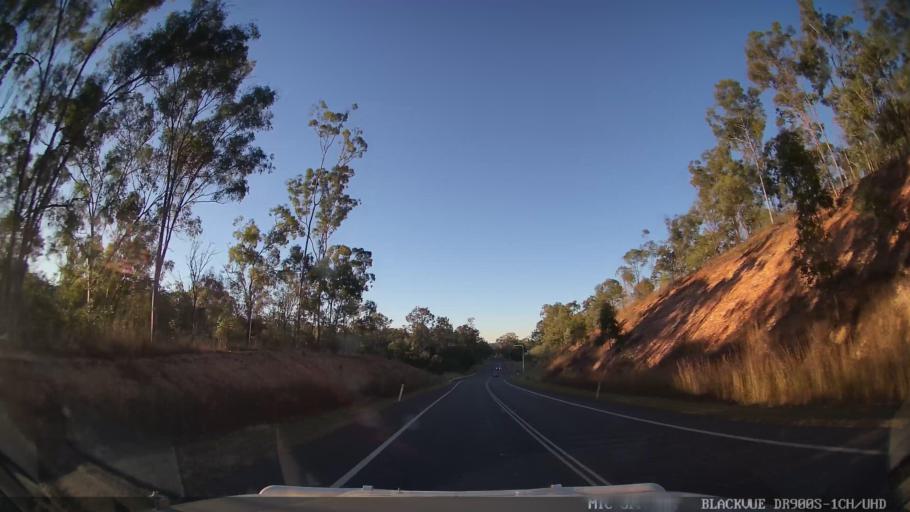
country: AU
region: Queensland
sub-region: Gladstone
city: Toolooa
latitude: -23.9626
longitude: 151.2177
